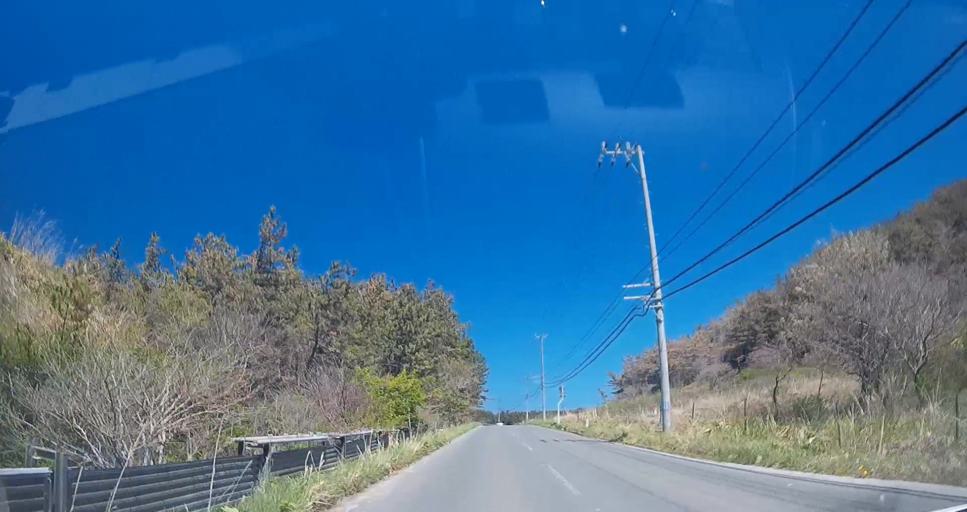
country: JP
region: Aomori
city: Mutsu
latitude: 41.4117
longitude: 141.4446
